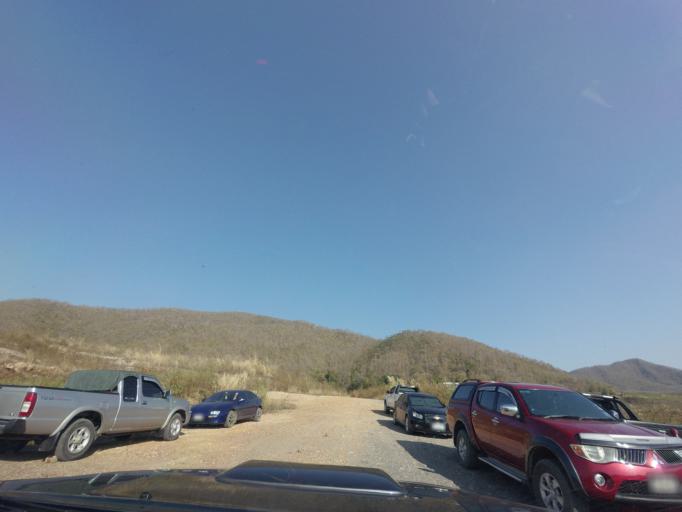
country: TH
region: Chiang Mai
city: San Sai
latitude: 18.9439
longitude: 99.1359
